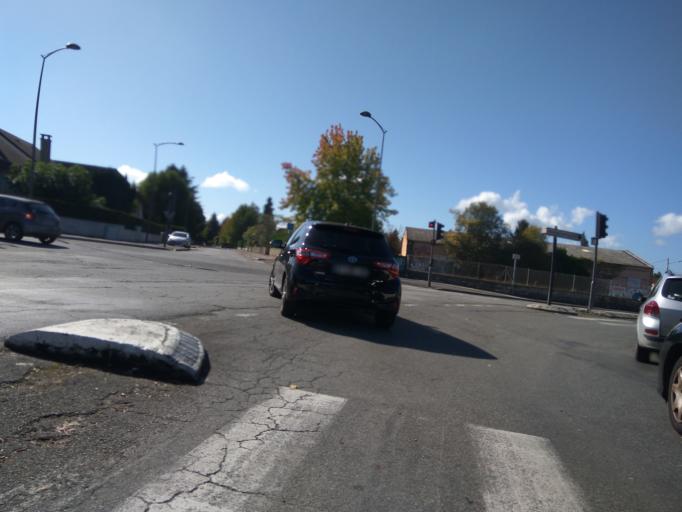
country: FR
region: Aquitaine
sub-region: Departement des Pyrenees-Atlantiques
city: Idron
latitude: 43.3026
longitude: -0.3297
